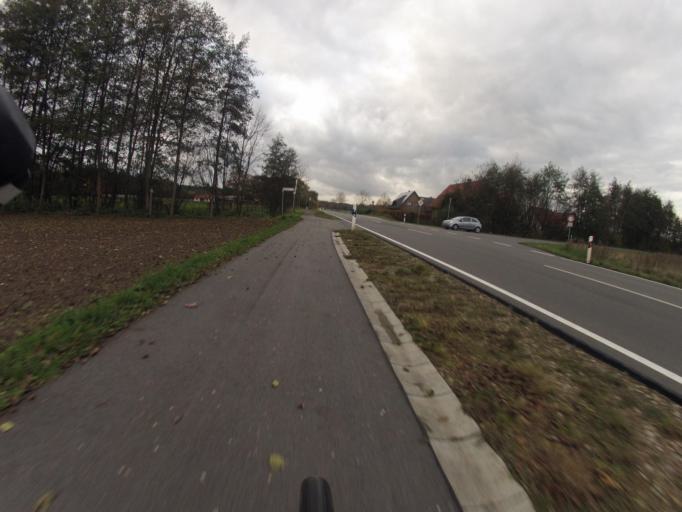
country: DE
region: North Rhine-Westphalia
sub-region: Regierungsbezirk Munster
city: Birgte
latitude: 52.2787
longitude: 7.6523
